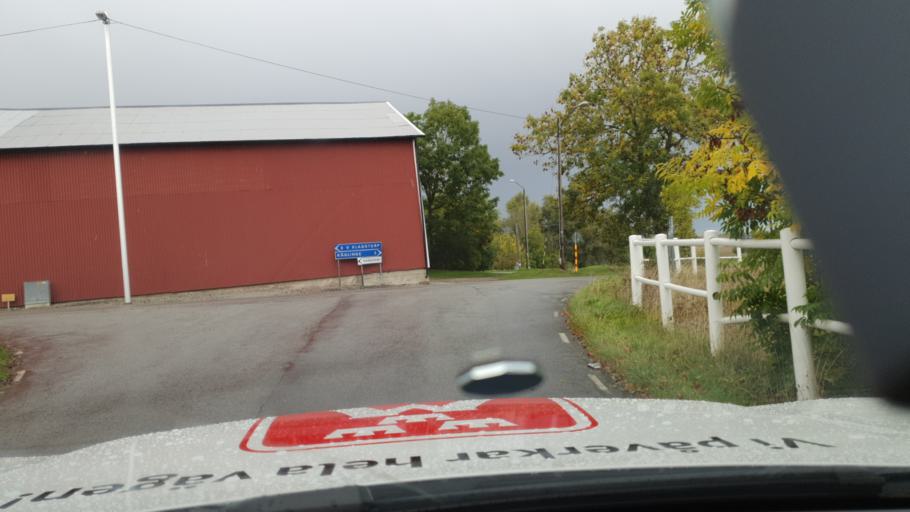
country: SE
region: Skane
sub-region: Malmo
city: Tygelsjo
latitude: 55.5246
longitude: 13.0415
